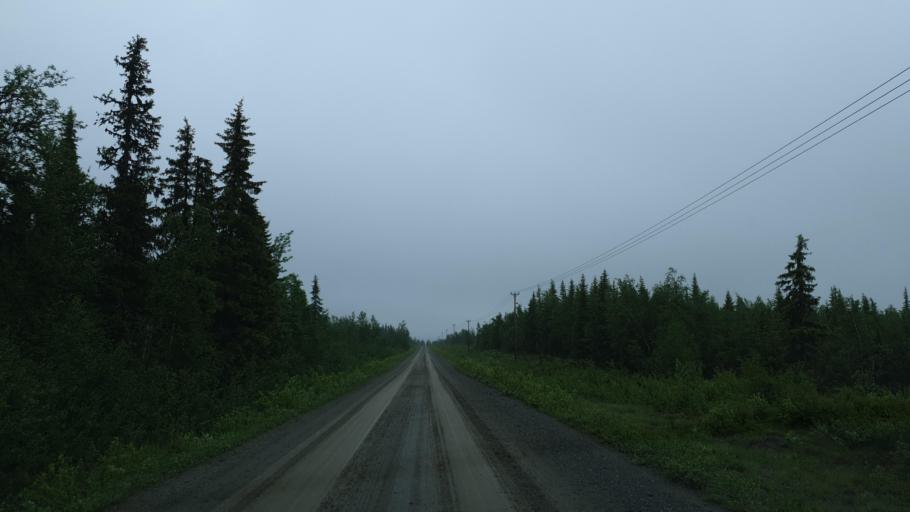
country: SE
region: Vaesterbotten
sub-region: Vilhelmina Kommun
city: Sjoberg
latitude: 65.3150
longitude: 15.9578
